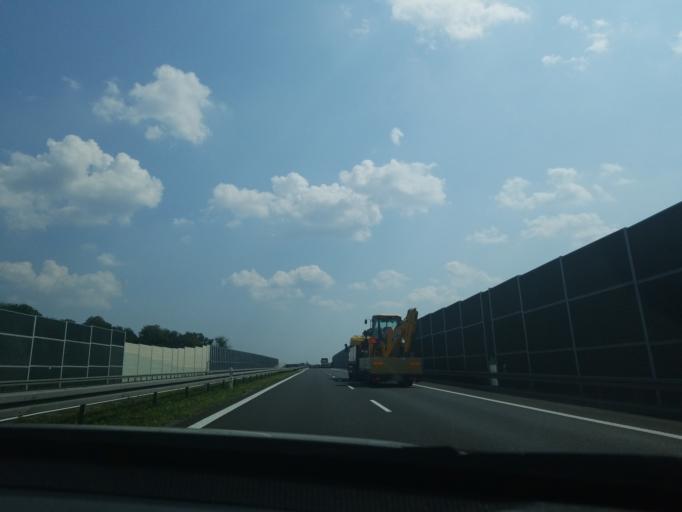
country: PL
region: Lesser Poland Voivodeship
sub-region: Powiat tarnowski
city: Lukowa
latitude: 50.0595
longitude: 20.9931
